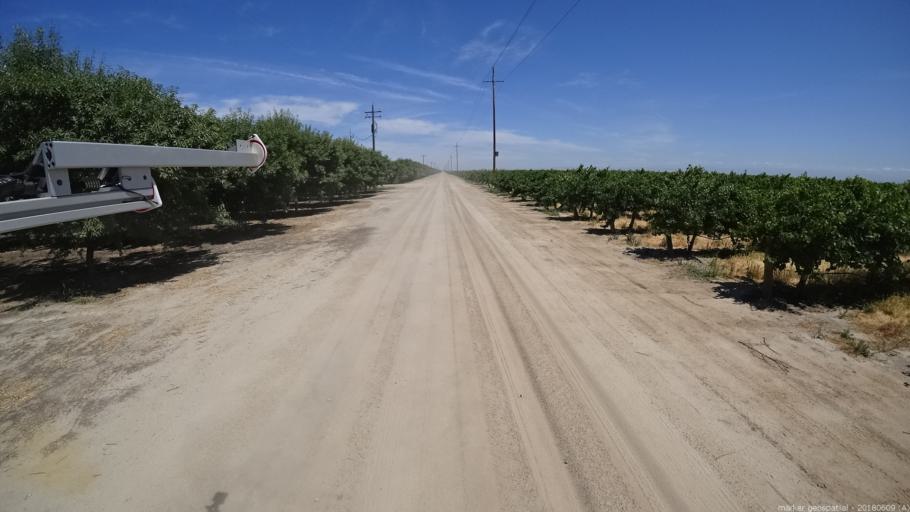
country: US
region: California
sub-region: Fresno County
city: Firebaugh
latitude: 36.9558
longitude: -120.3280
